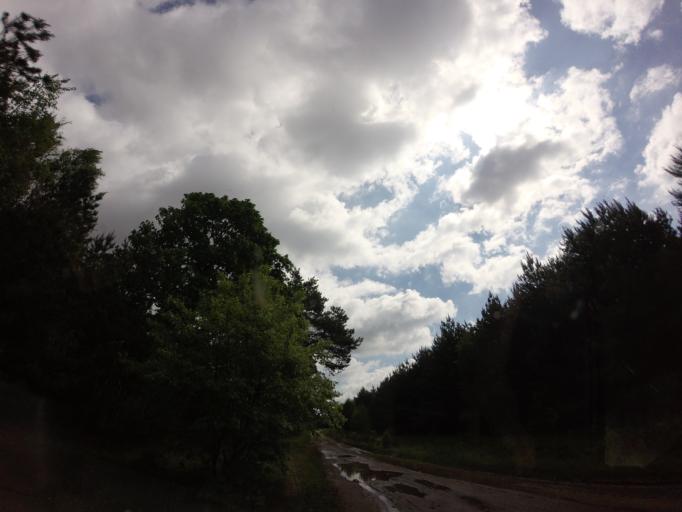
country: PL
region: West Pomeranian Voivodeship
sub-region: Powiat choszczenski
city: Drawno
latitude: 53.1782
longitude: 15.6909
